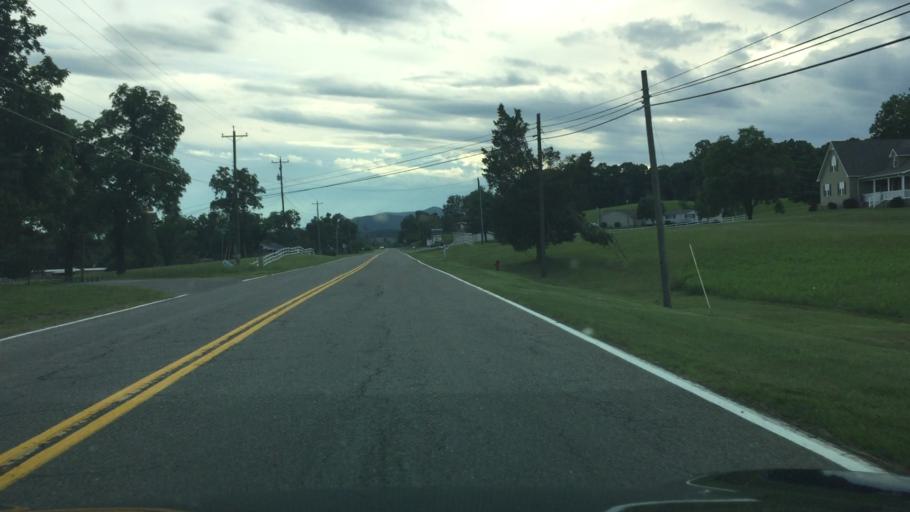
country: US
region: Virginia
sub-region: Pulaski County
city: Pulaski
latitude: 36.9545
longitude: -80.8781
